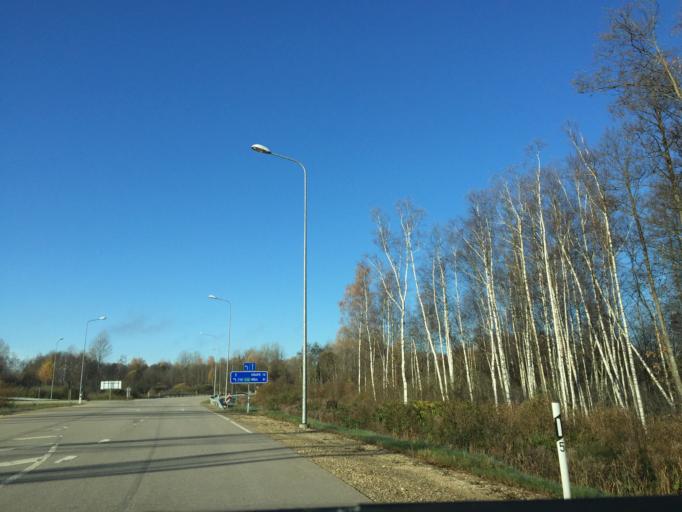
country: LV
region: Aizkraukles Rajons
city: Aizkraukle
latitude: 56.7046
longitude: 25.2778
